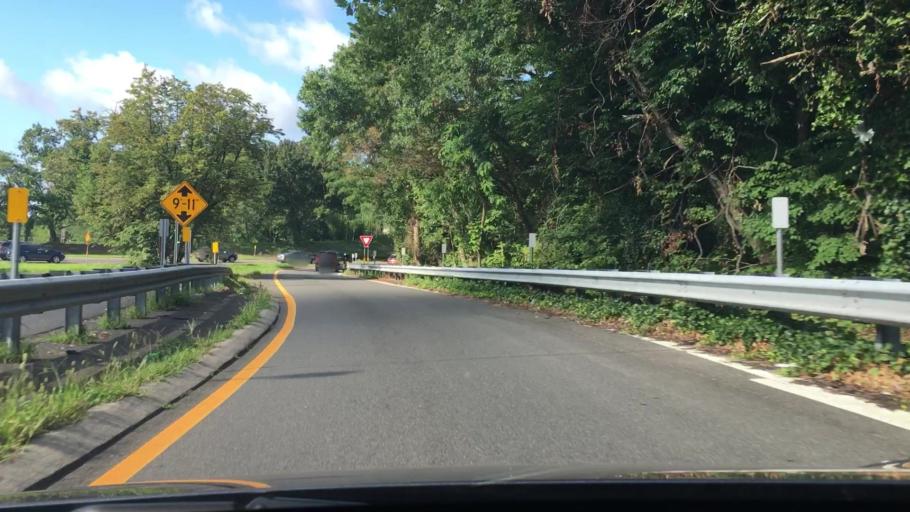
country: US
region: New York
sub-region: Nassau County
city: Plainedge
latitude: 40.7021
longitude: -73.4915
